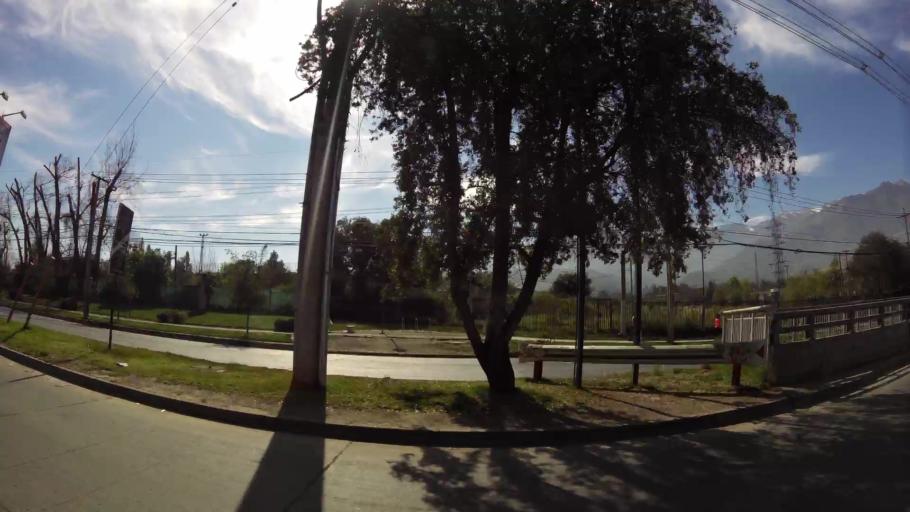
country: CL
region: Santiago Metropolitan
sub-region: Provincia de Santiago
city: Villa Presidente Frei, Nunoa, Santiago, Chile
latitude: -33.4331
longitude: -70.5383
